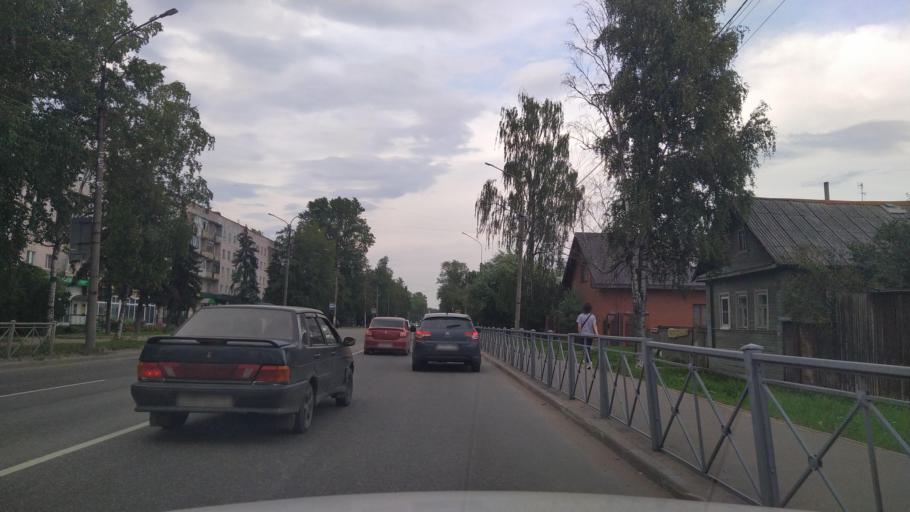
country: RU
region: Novgorod
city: Velikiy Novgorod
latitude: 58.5188
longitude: 31.2508
